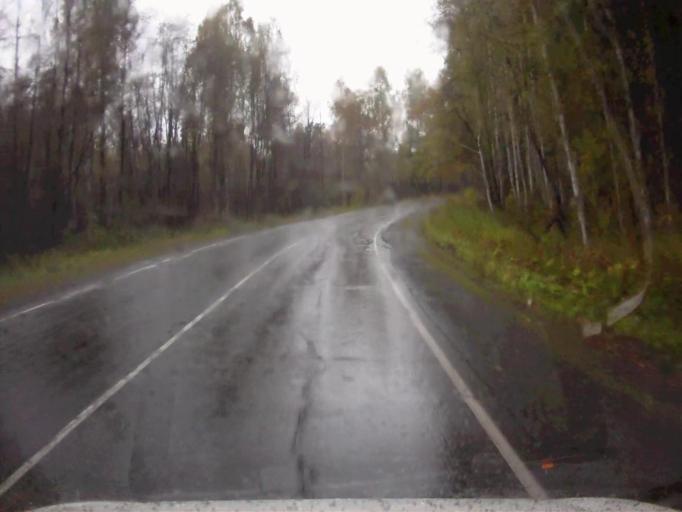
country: RU
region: Chelyabinsk
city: Kyshtym
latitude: 55.9065
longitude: 60.4406
